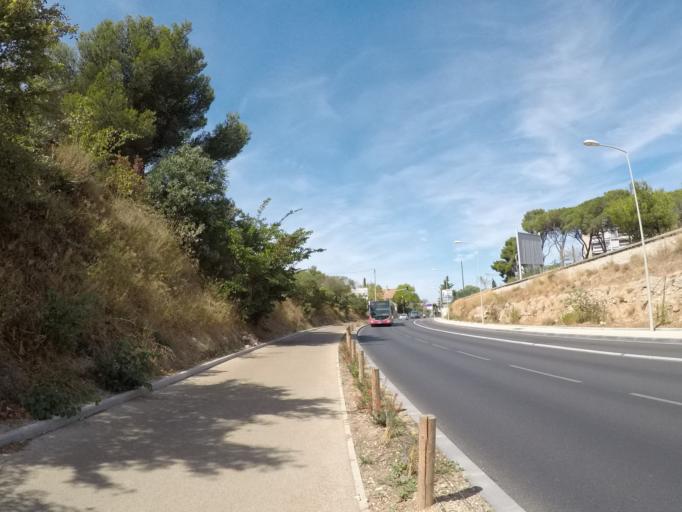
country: FR
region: Provence-Alpes-Cote d'Azur
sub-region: Departement des Bouches-du-Rhone
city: Marseille 09
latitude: 43.2456
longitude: 5.4101
